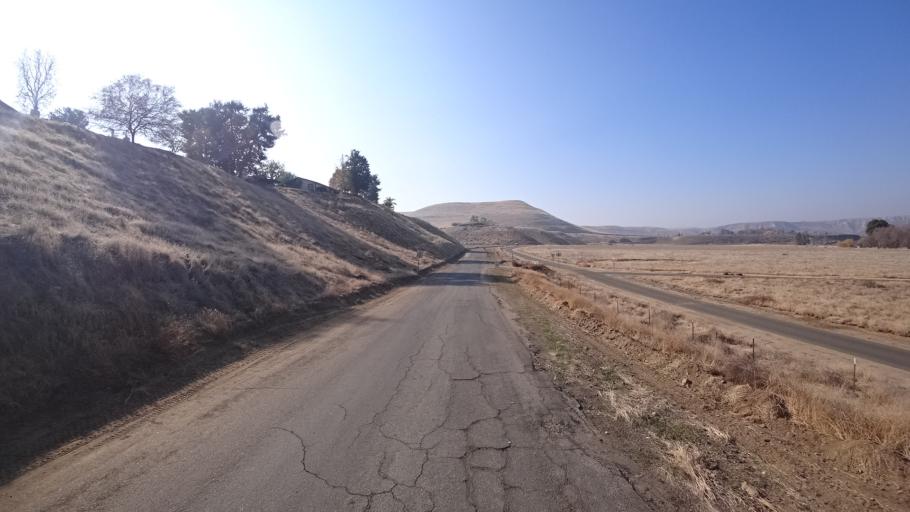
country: US
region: California
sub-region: Kern County
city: Oildale
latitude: 35.4335
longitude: -118.8759
